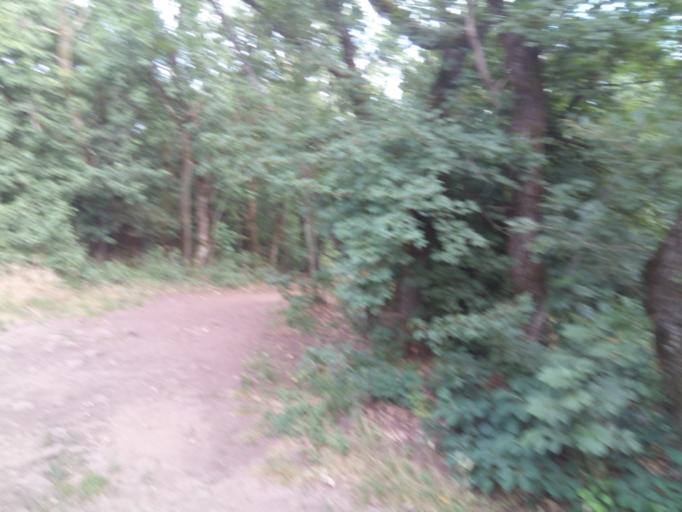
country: HU
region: Veszprem
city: Csopak
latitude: 46.9971
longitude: 17.9688
